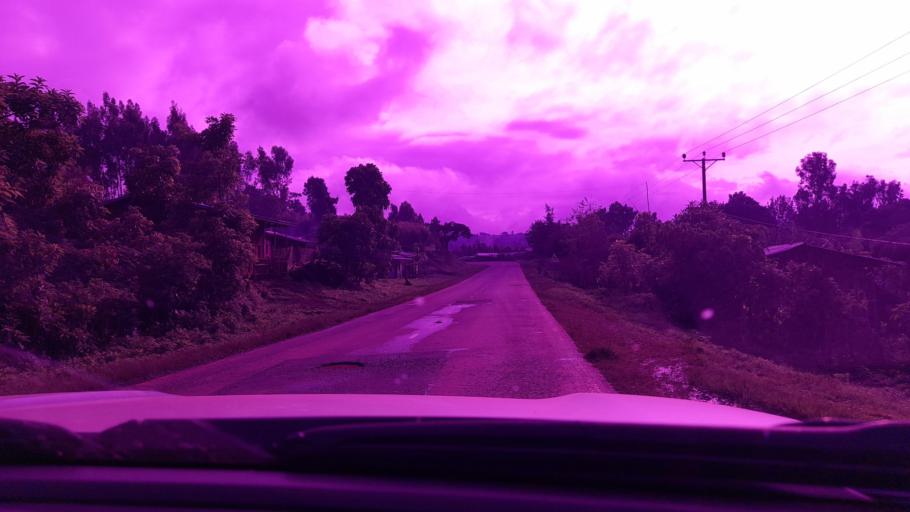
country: ET
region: Oromiya
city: Bedele
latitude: 8.2269
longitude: 36.4496
